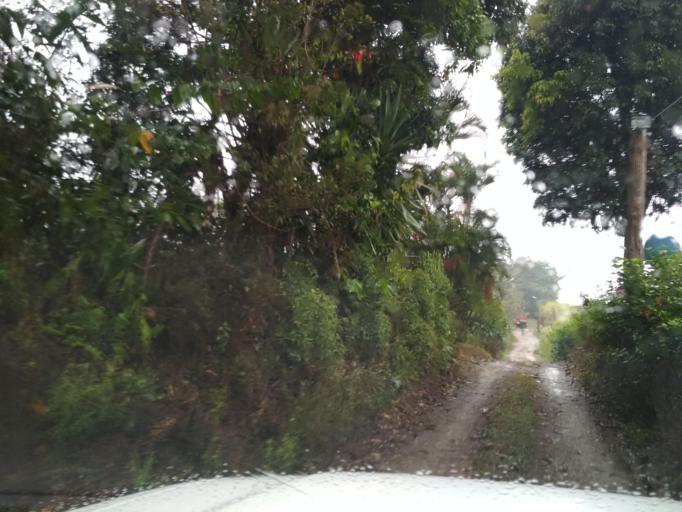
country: MX
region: Veracruz
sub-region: Amatlan de los Reyes
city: Centro de Readaptacion Social
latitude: 18.8284
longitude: -96.9338
